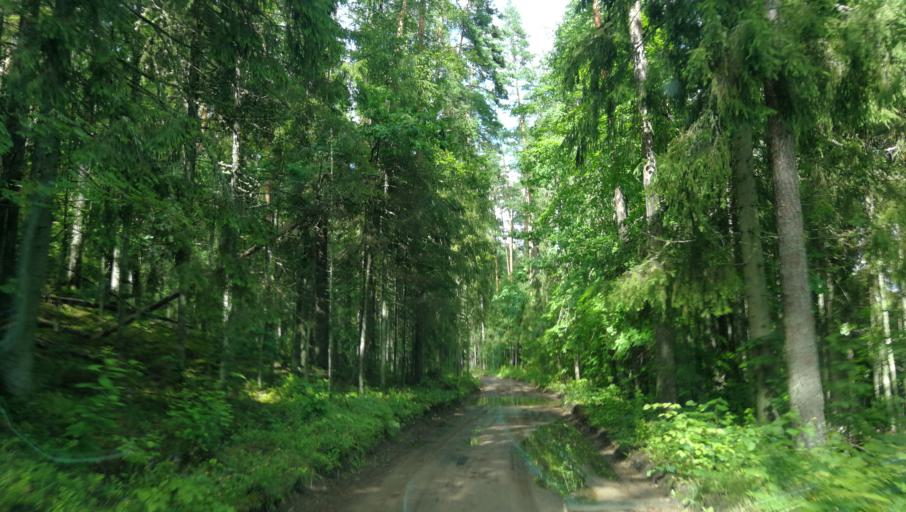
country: LV
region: Cesu Rajons
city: Cesis
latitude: 57.3064
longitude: 25.2128
